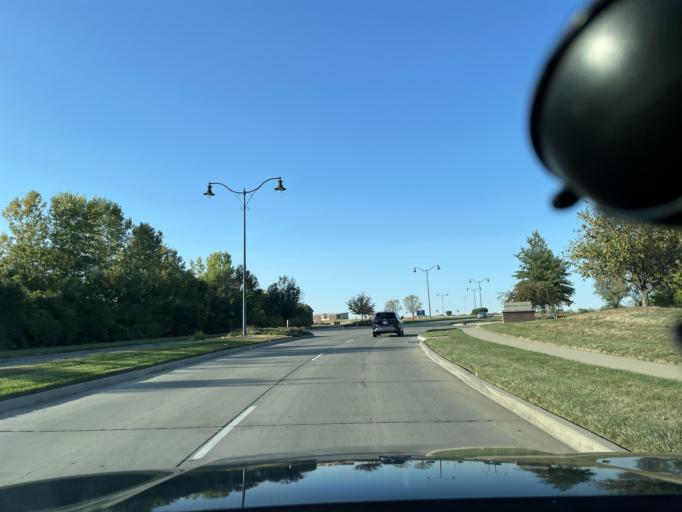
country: US
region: Missouri
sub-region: Andrew County
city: Country Club Village
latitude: 39.8131
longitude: -94.8074
